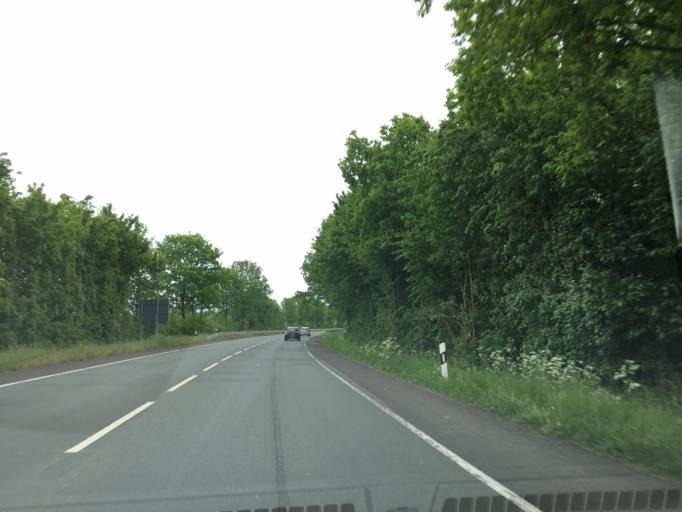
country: DE
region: North Rhine-Westphalia
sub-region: Regierungsbezirk Munster
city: Senden
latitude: 51.9219
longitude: 7.4762
